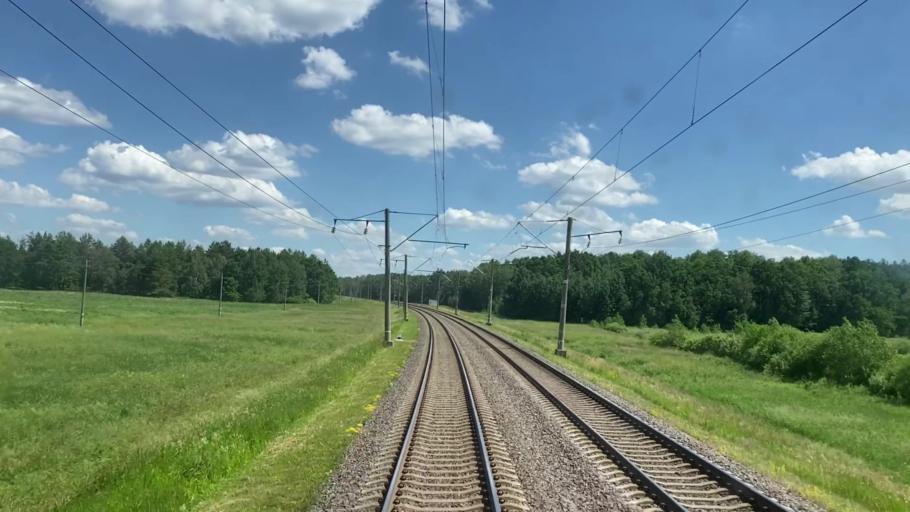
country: BY
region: Brest
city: Ivatsevichy
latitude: 52.8428
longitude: 25.5529
